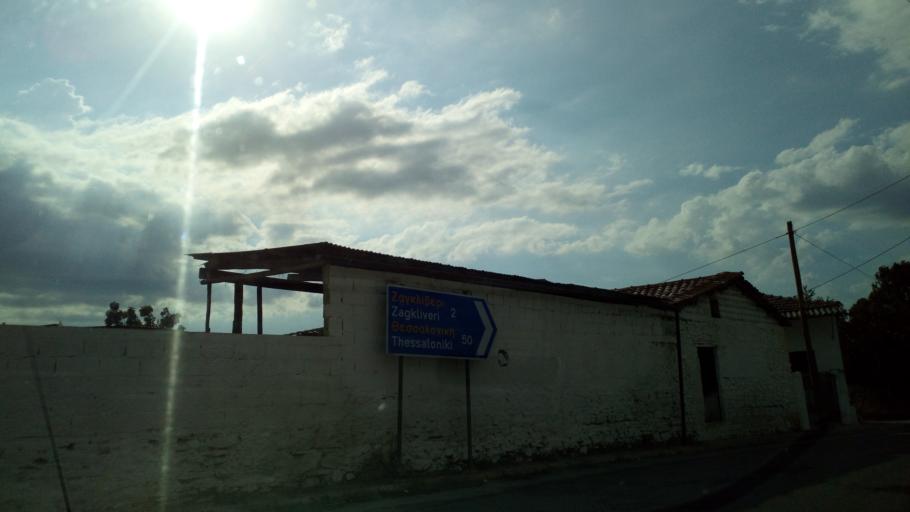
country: GR
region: Central Macedonia
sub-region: Nomos Chalkidikis
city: Galatista
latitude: 40.5553
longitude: 23.3018
